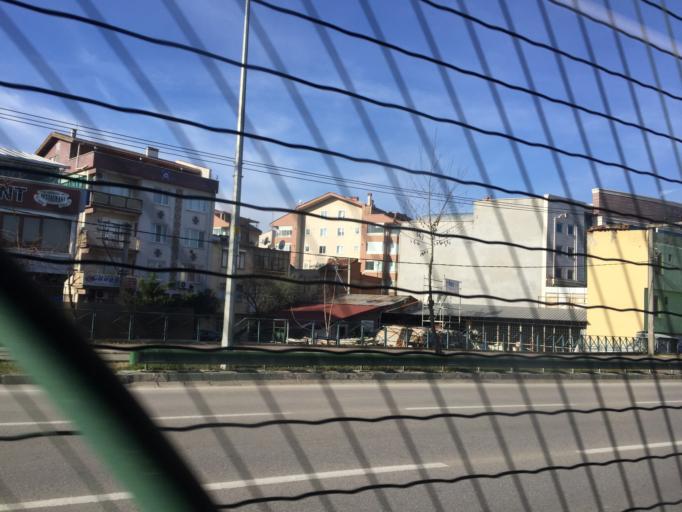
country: TR
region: Bursa
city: Yildirim
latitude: 40.2162
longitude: 29.0009
